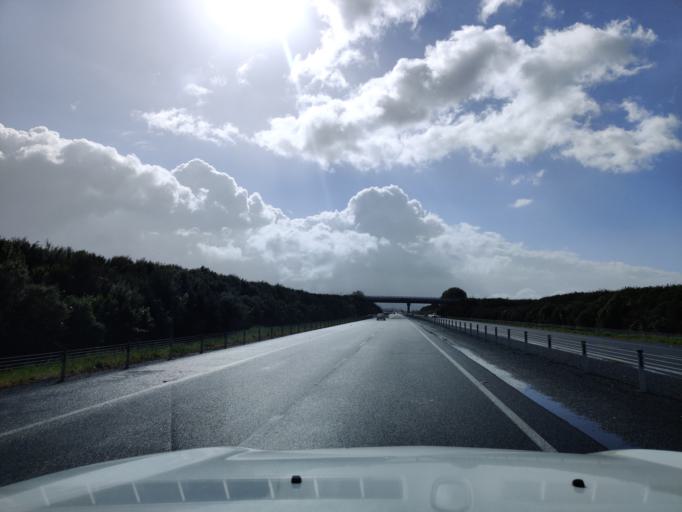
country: NZ
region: Waikato
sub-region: Waipa District
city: Cambridge
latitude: -37.8688
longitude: 175.4361
